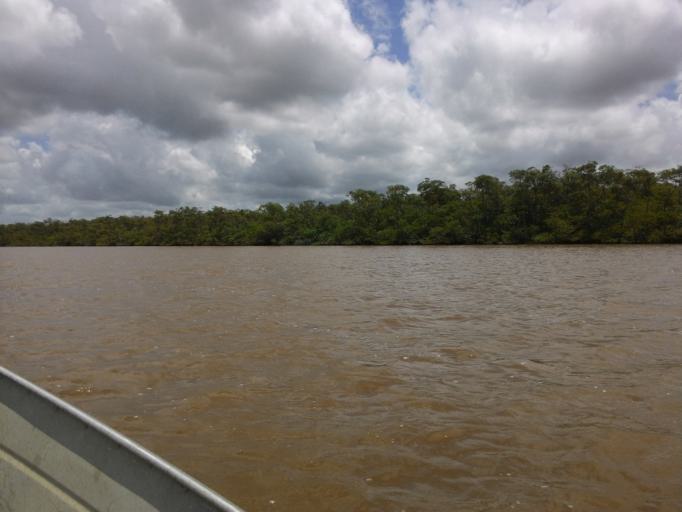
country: BR
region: Sao Paulo
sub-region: Pariquera-Acu
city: Pariquera Acu
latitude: -24.8329
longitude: -47.7363
